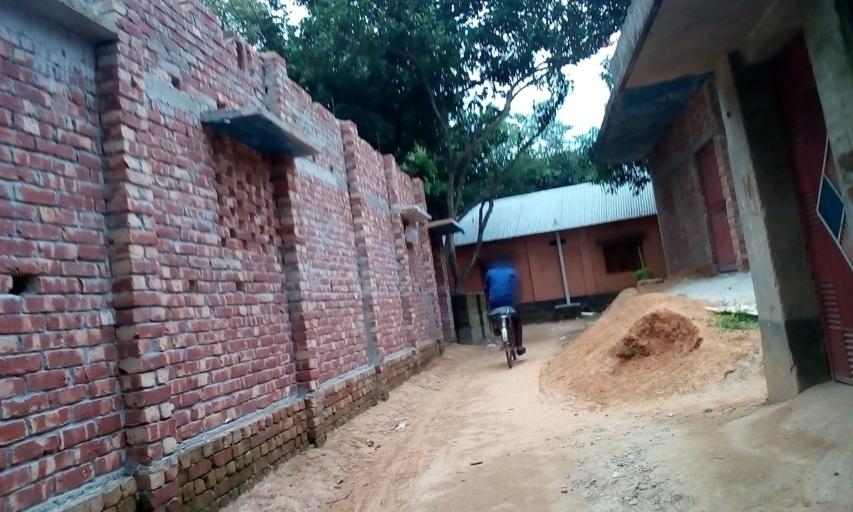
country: IN
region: West Bengal
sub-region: Dakshin Dinajpur
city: Balurghat
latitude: 25.3844
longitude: 88.9954
